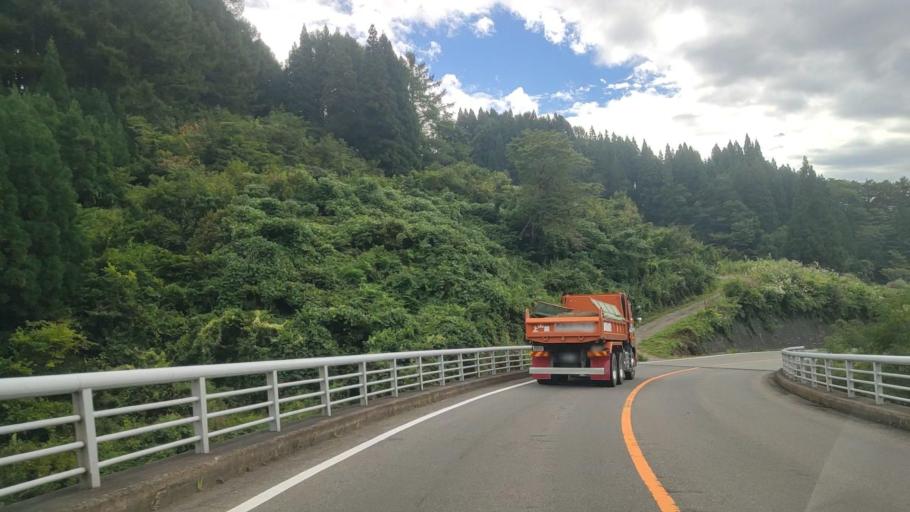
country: JP
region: Nagano
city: Iiyama
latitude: 36.8733
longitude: 138.3219
